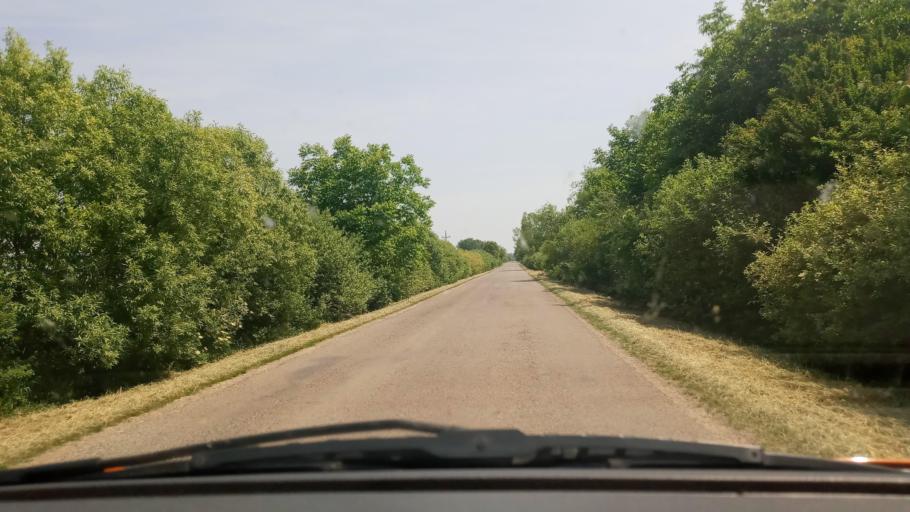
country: HU
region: Baranya
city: Szigetvar
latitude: 45.9660
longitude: 17.6915
